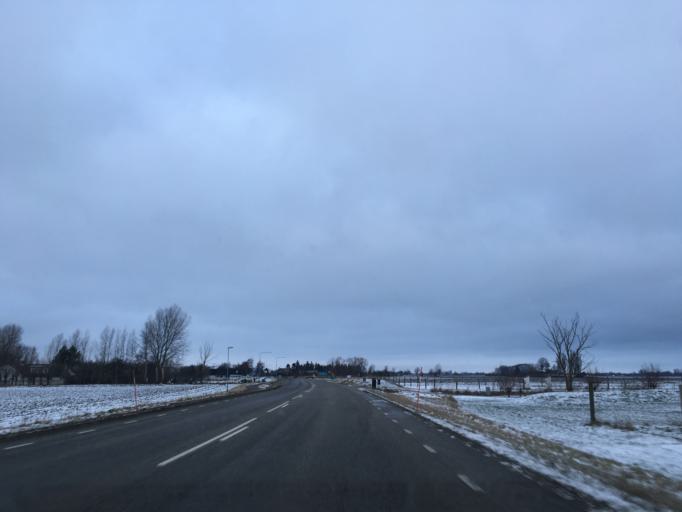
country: SE
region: Skane
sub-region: Vellinge Kommun
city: Hollviken
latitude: 55.4330
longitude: 12.9842
